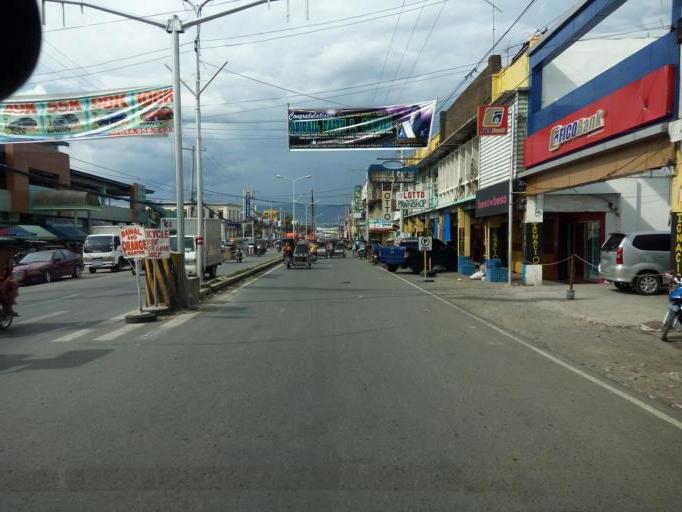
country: PH
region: Central Luzon
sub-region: Province of Nueva Ecija
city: Sibul
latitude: 15.7932
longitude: 120.9912
